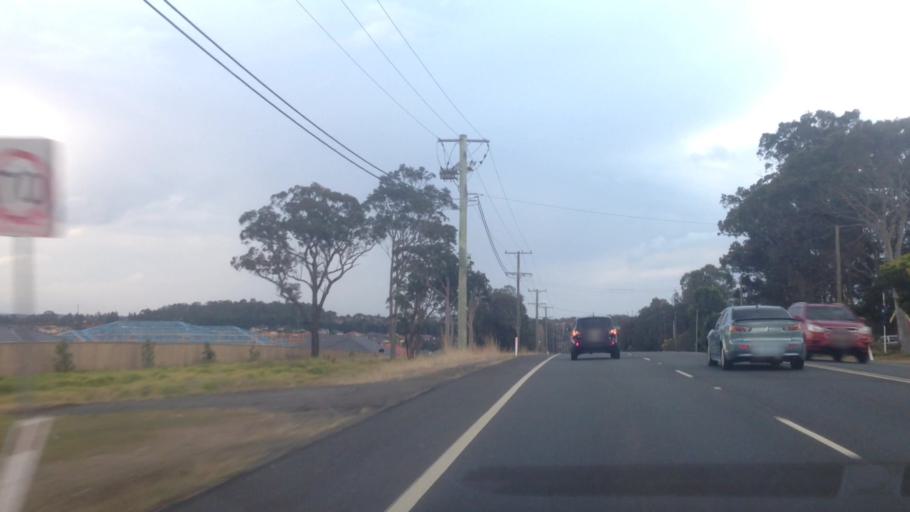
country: AU
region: New South Wales
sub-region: Wyong Shire
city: Kanwal
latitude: -33.2593
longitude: 151.4850
